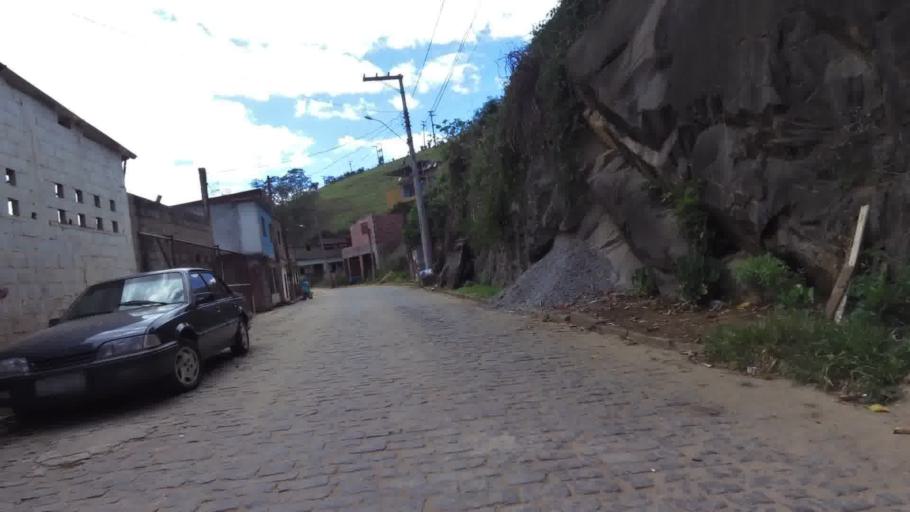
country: BR
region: Espirito Santo
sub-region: Rio Novo Do Sul
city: Rio Novo do Sul
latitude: -20.8683
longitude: -40.9383
